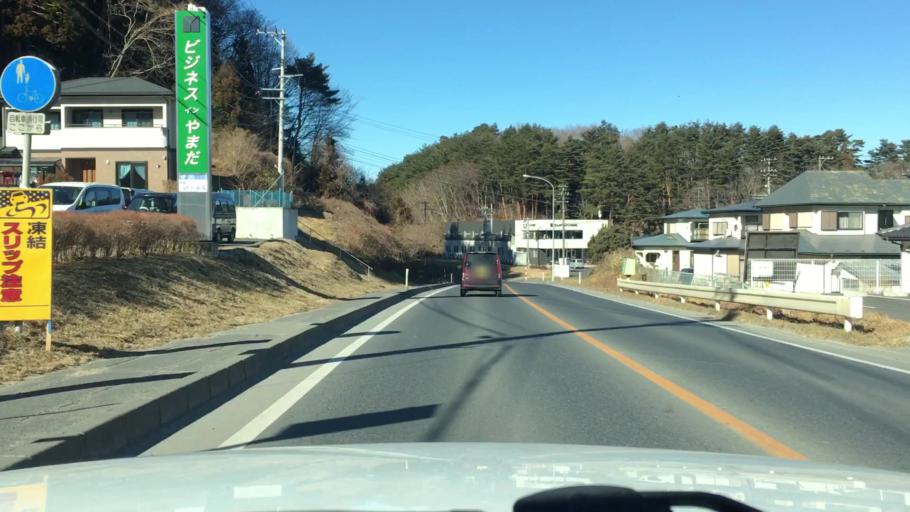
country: JP
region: Iwate
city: Yamada
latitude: 39.4447
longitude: 141.9702
